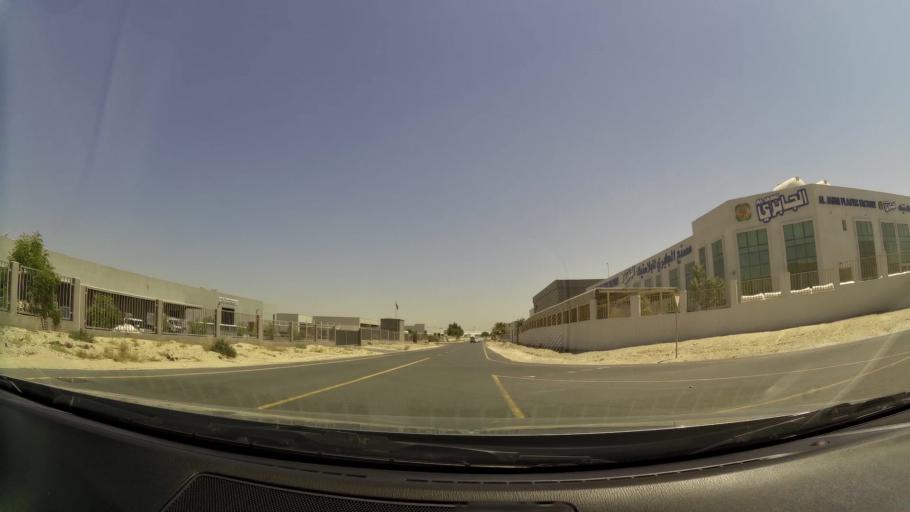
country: AE
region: Dubai
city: Dubai
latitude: 24.9761
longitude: 55.1897
